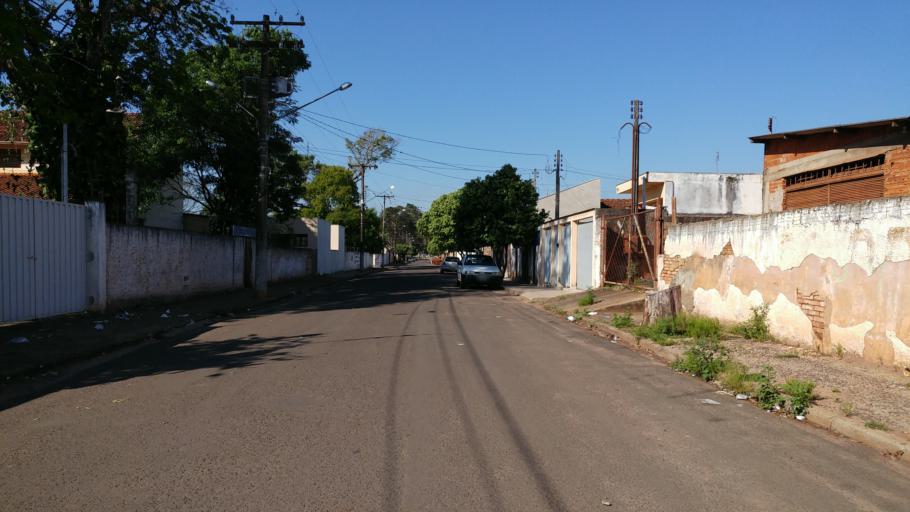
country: BR
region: Sao Paulo
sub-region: Paraguacu Paulista
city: Paraguacu Paulista
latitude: -22.4185
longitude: -50.5704
